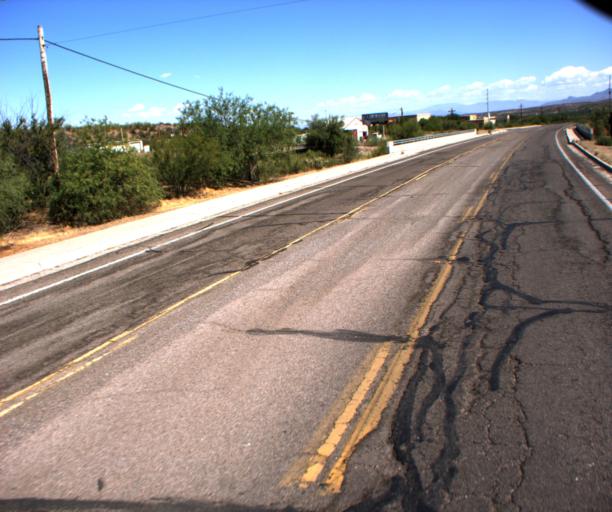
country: US
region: Arizona
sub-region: Pinal County
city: Mammoth
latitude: 32.7358
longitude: -110.6488
